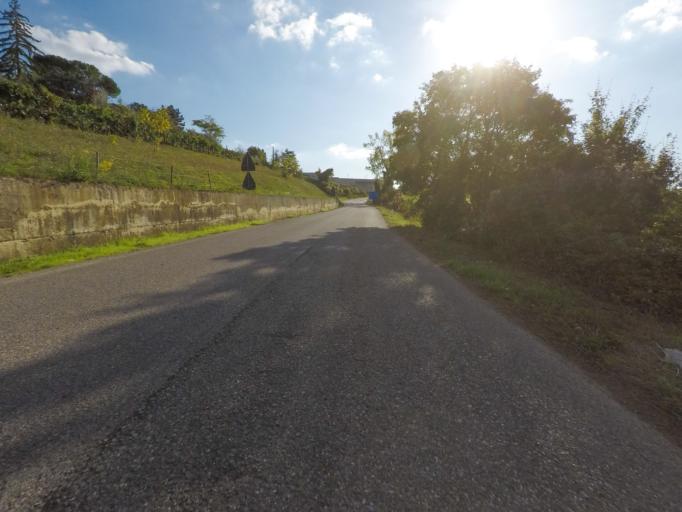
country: IT
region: Tuscany
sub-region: Provincia di Siena
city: Radda in Chianti
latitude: 43.4920
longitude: 11.3876
